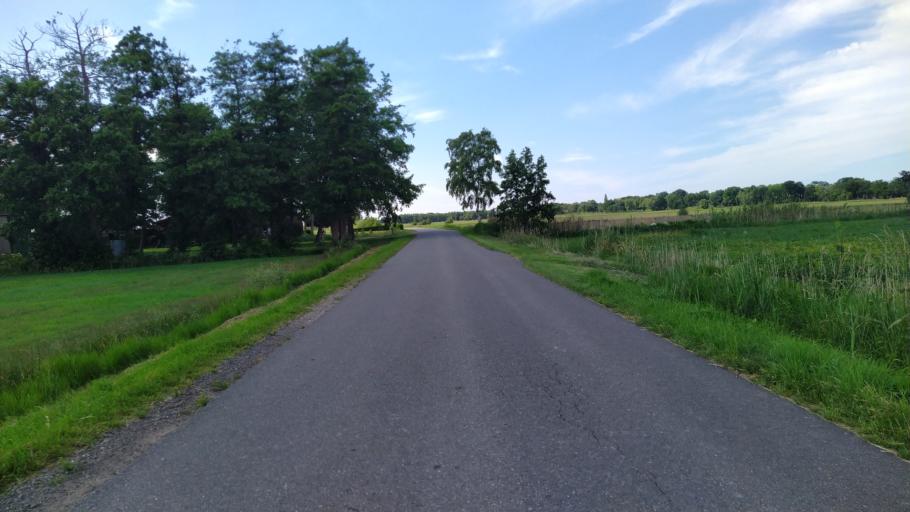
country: DE
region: Lower Saxony
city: Odisheim
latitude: 53.6644
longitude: 8.9292
